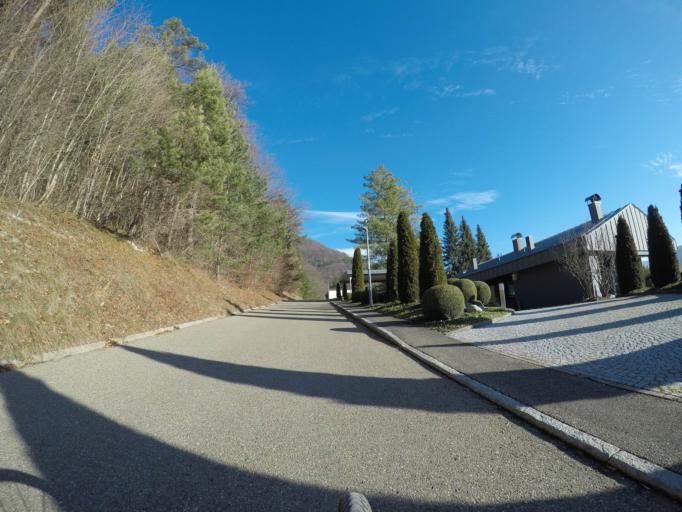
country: DE
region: Baden-Wuerttemberg
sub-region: Tuebingen Region
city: Pfullingen
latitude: 48.4481
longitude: 9.2557
